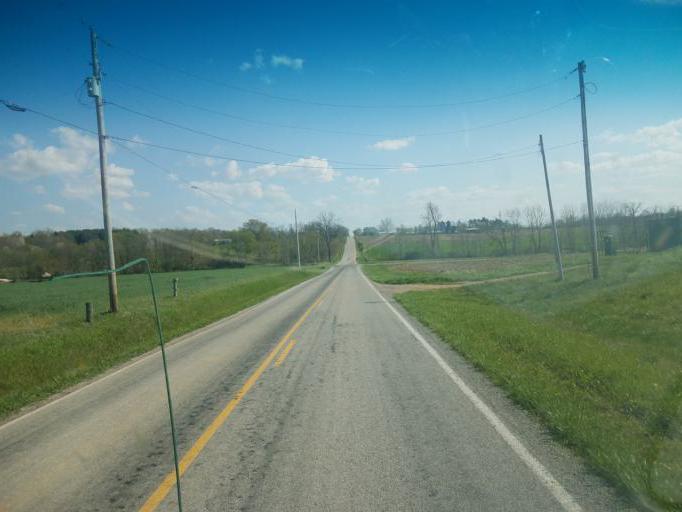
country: US
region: Ohio
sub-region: Wayne County
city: Creston
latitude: 40.9600
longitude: -81.9572
